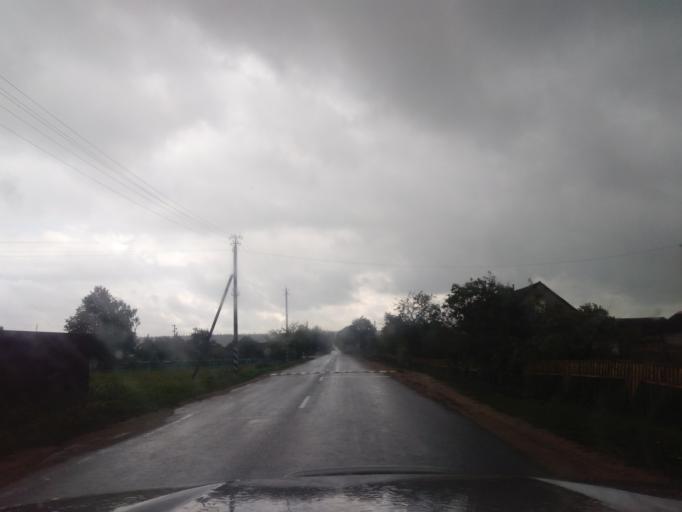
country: BY
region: Minsk
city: Tsimkavichy
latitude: 53.1756
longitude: 26.9588
